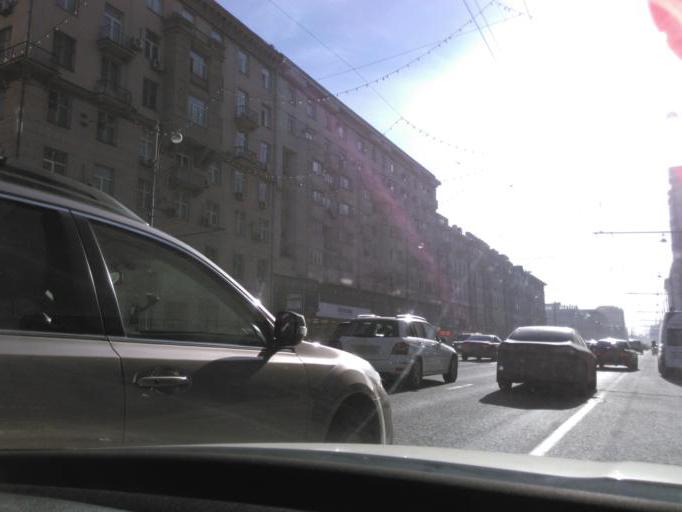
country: RU
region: Moscow
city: Moscow
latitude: 55.7723
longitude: 37.5918
